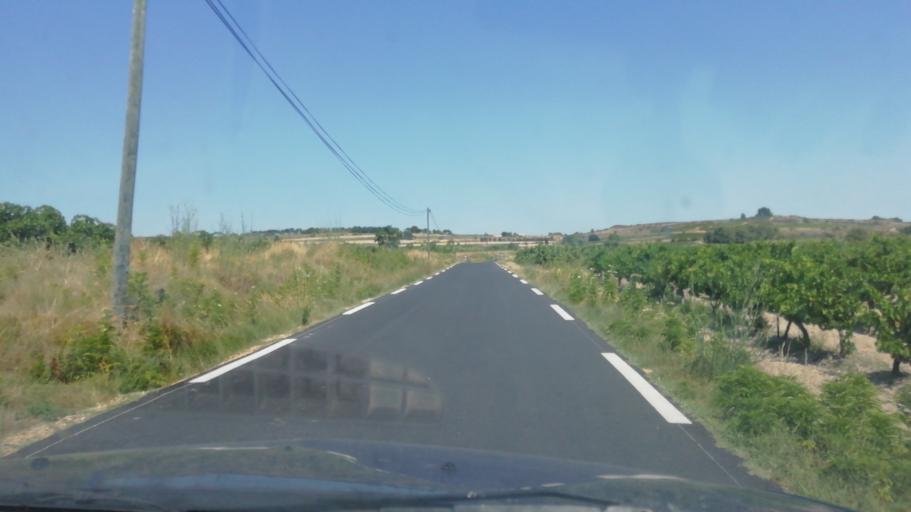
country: FR
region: Languedoc-Roussillon
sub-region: Departement de l'Herault
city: Capestang
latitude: 43.3325
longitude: 3.0585
